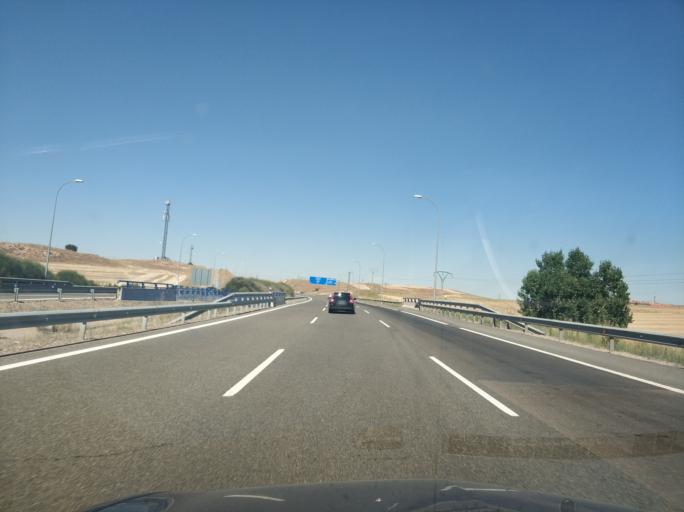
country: ES
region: Castille and Leon
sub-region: Provincia de Salamanca
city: Villamayor
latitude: 40.9716
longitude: -5.6953
